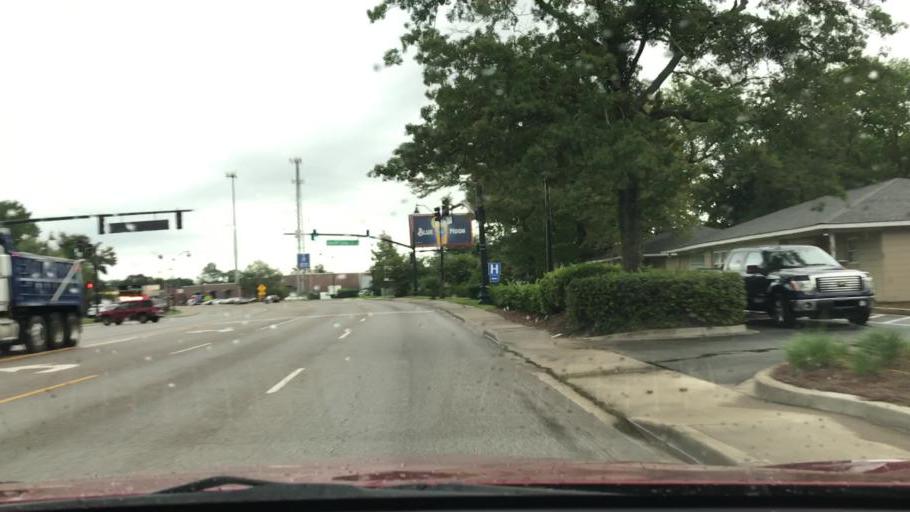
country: US
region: South Carolina
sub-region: Charleston County
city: North Charleston
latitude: 32.8637
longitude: -80.0172
